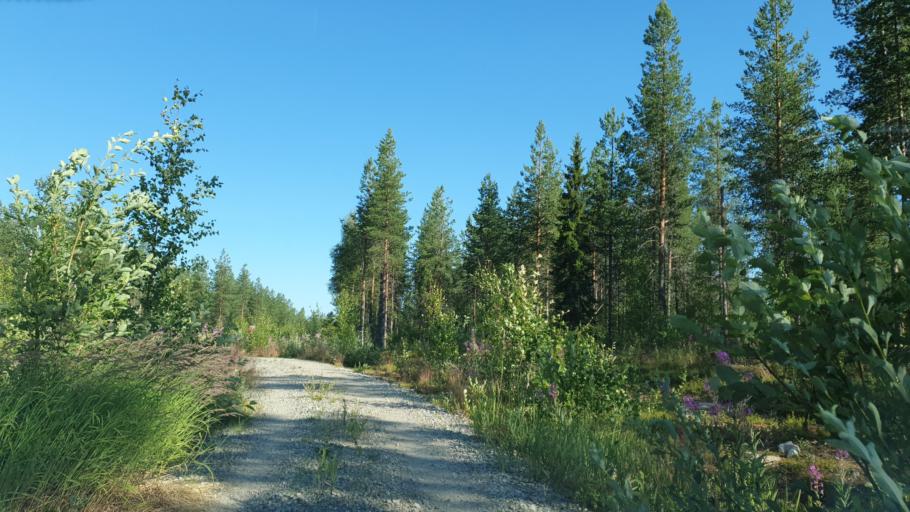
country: FI
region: Kainuu
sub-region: Kehys-Kainuu
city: Kuhmo
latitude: 64.0016
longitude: 29.7501
